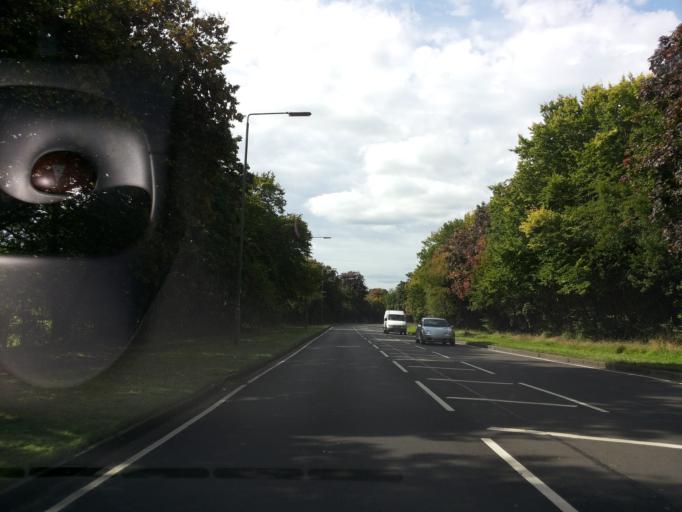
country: GB
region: England
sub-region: Greater London
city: Orpington
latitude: 51.3453
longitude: 0.0964
